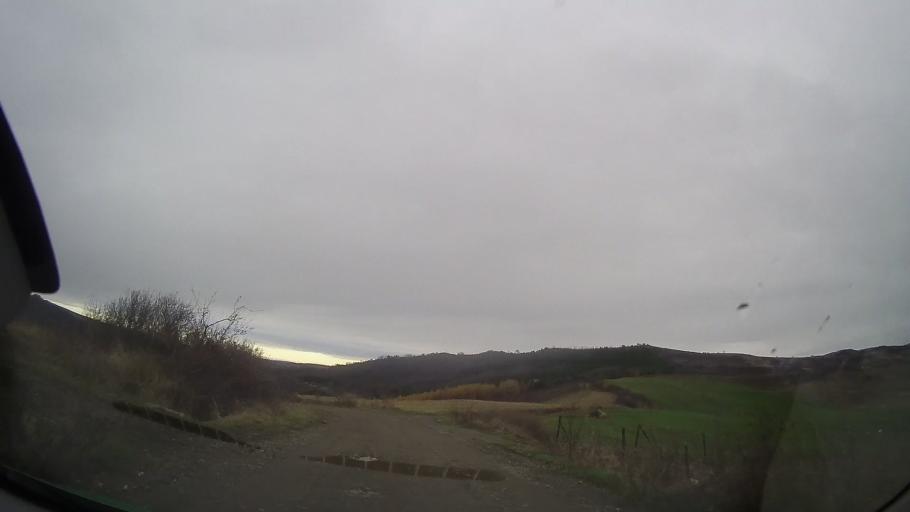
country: RO
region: Mures
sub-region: Comuna Bala
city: Bala
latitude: 46.6749
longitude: 24.4842
